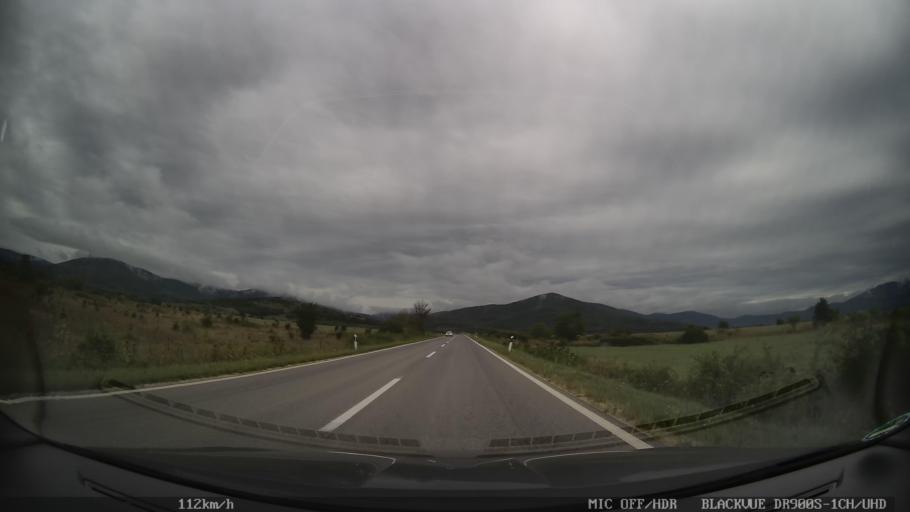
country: HR
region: Licko-Senjska
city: Otocac
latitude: 44.8600
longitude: 15.3117
